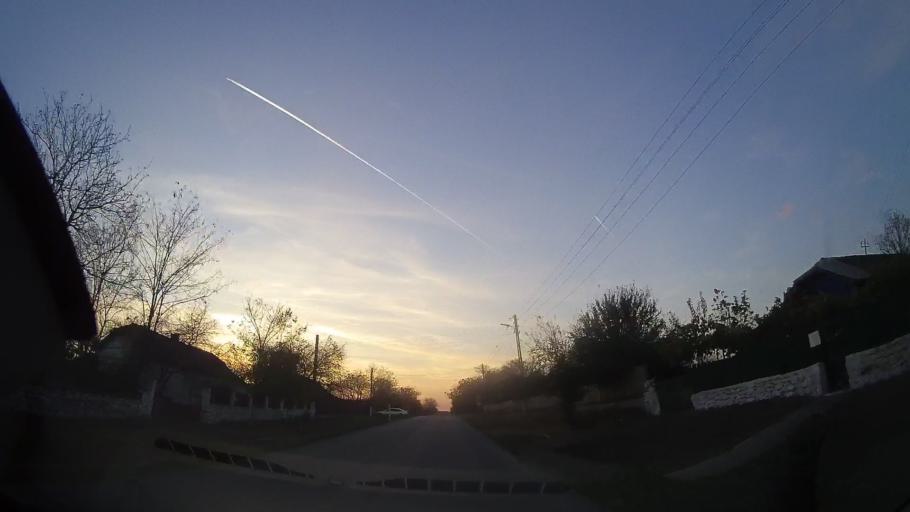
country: RO
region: Constanta
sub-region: Comuna Mereni
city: Mereni
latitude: 44.0156
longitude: 28.3172
